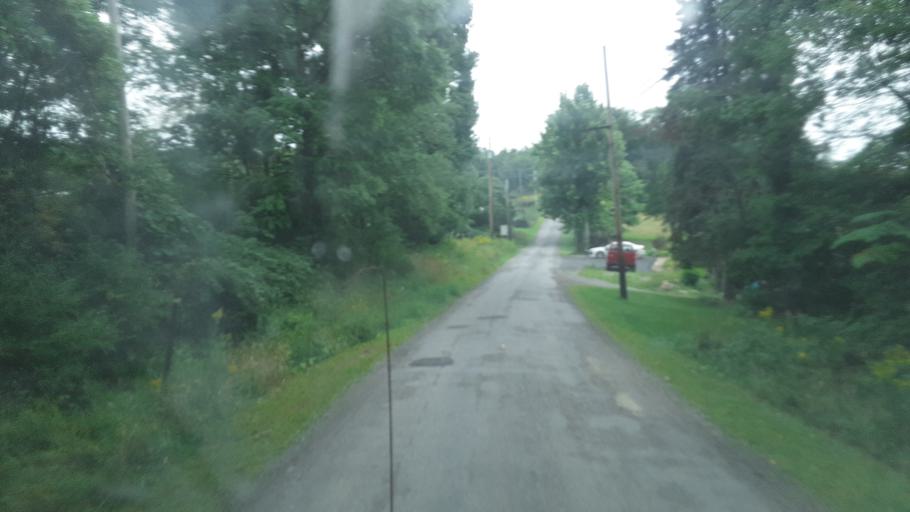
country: US
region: Pennsylvania
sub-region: Jefferson County
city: Punxsutawney
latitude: 40.9587
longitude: -79.1217
